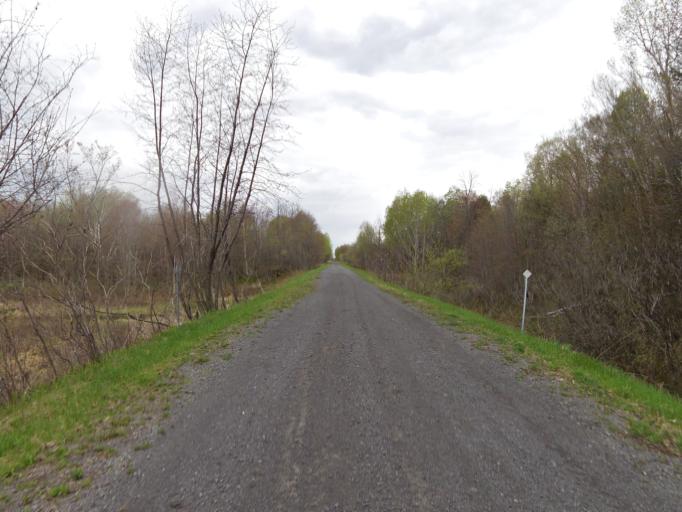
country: CA
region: Quebec
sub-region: Outaouais
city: Papineauville
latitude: 45.5177
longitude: -74.9502
